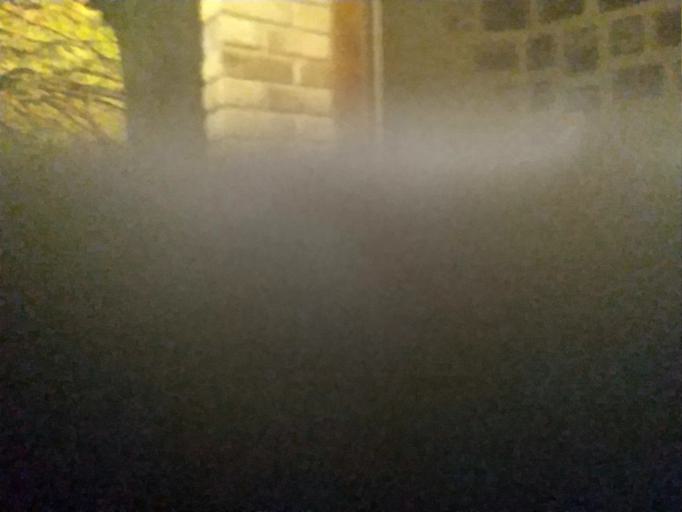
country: RU
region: Moskovskaya
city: Vysokovsk
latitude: 56.2635
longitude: 36.4871
